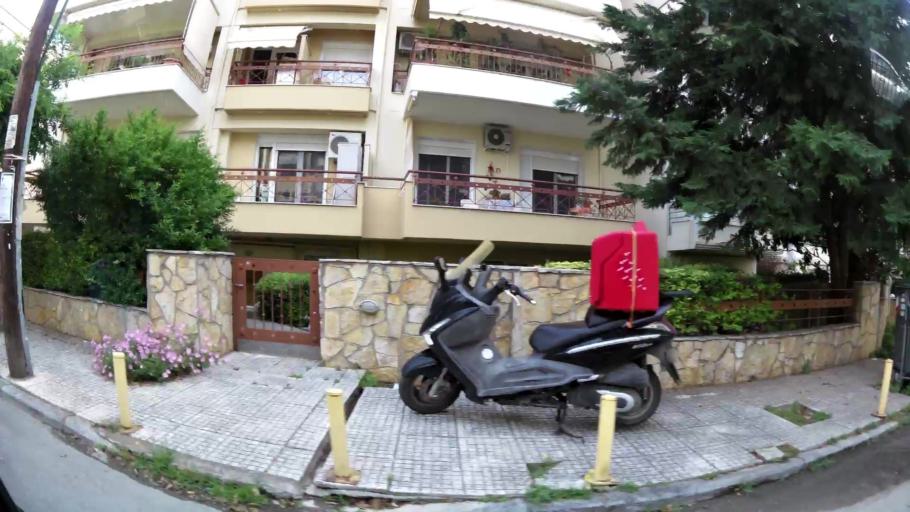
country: GR
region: Central Macedonia
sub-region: Nomos Thessalonikis
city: Thermi
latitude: 40.5467
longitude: 23.0164
